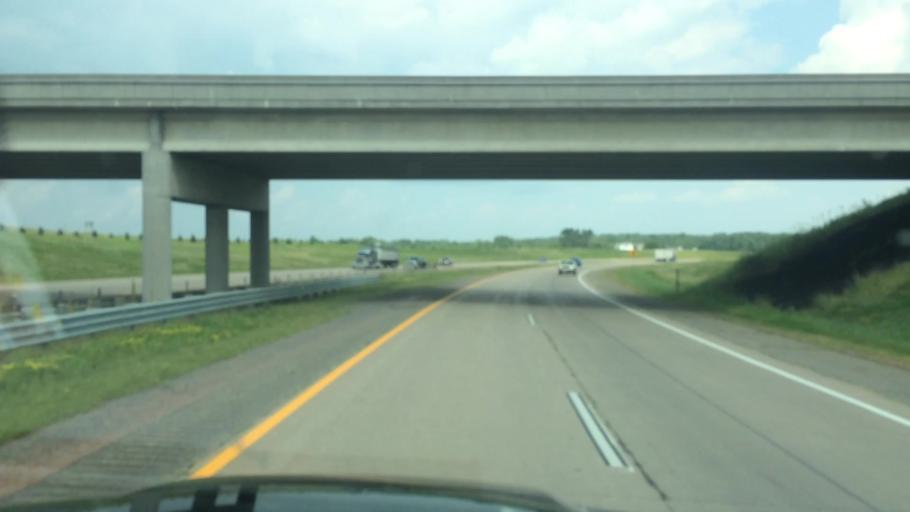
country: US
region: Wisconsin
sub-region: Clark County
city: Abbotsford
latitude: 44.9438
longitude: -90.2902
